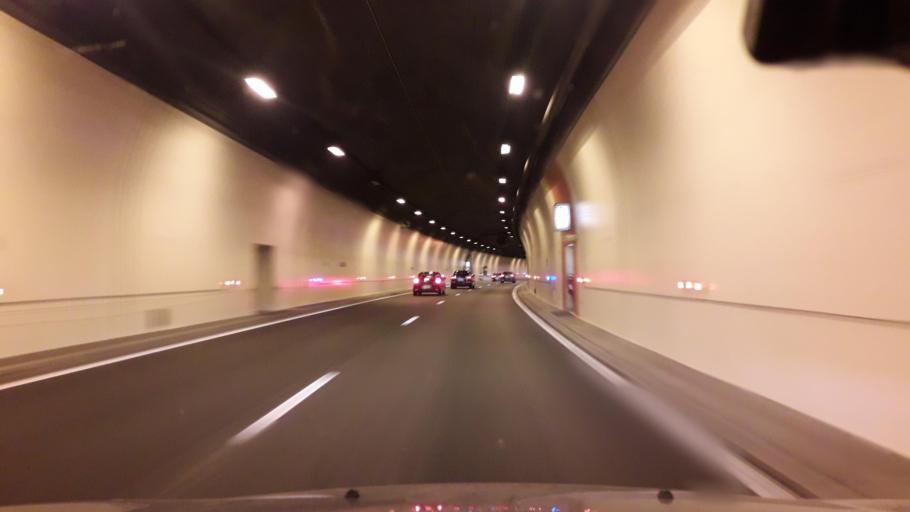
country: FR
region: Rhone-Alpes
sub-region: Departement du Rhone
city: Ecully
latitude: 45.7861
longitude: 4.8060
